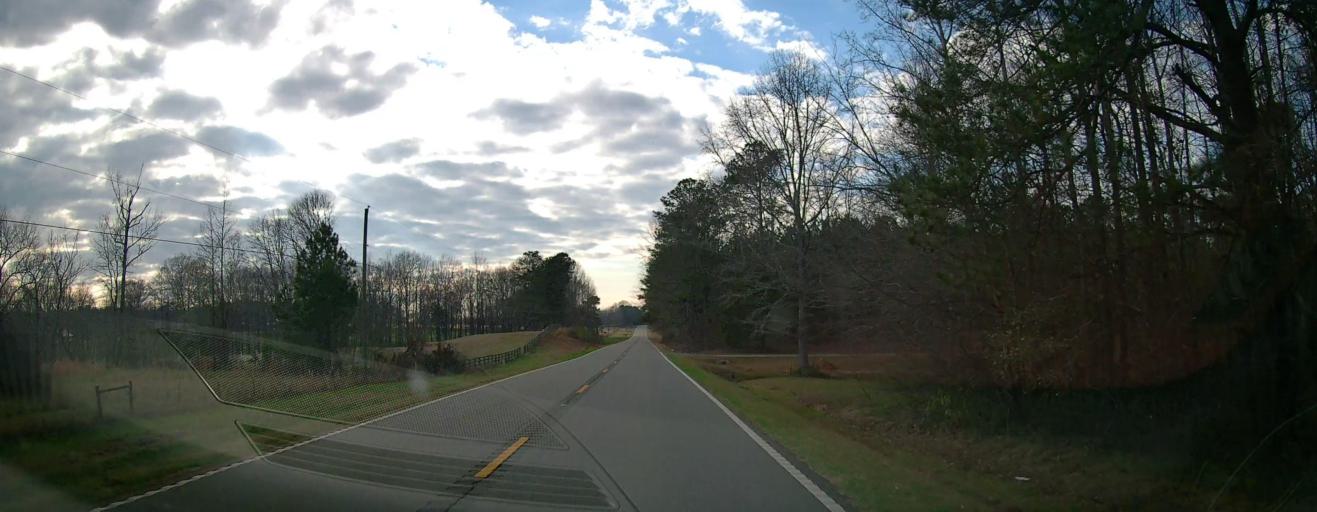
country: US
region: Georgia
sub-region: Harris County
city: Hamilton
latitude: 32.6844
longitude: -84.7607
